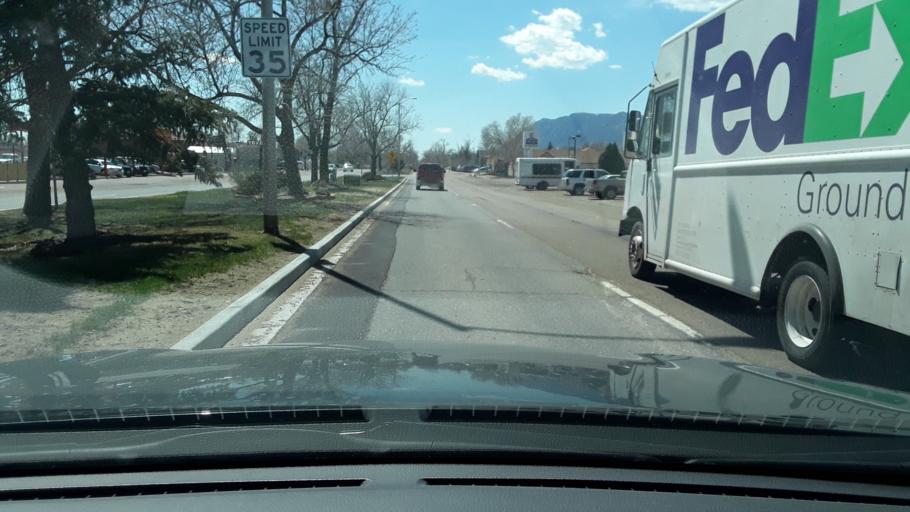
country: US
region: Colorado
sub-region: El Paso County
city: Colorado Springs
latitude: 38.8730
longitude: -104.8197
